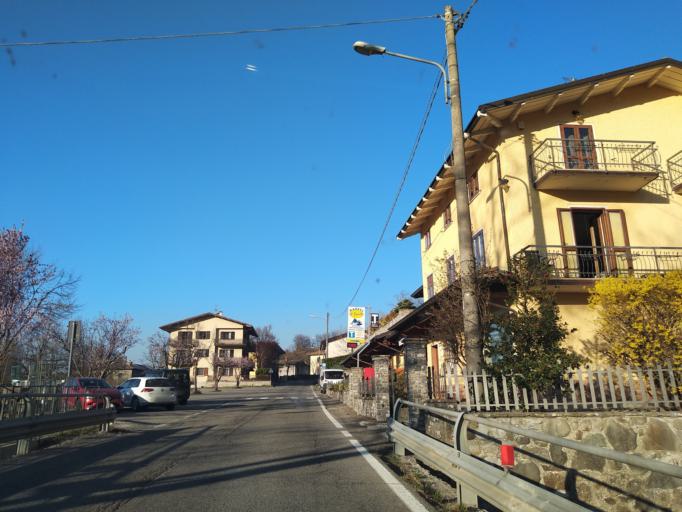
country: IT
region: Emilia-Romagna
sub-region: Provincia di Reggio Emilia
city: Ramiseto
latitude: 44.4116
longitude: 10.2834
